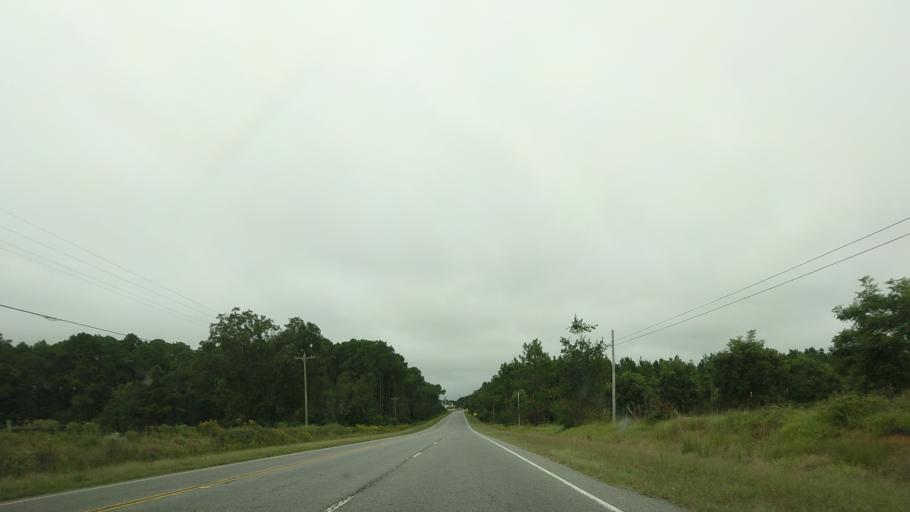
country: US
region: Georgia
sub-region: Irwin County
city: Ocilla
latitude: 31.6394
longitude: -83.2465
